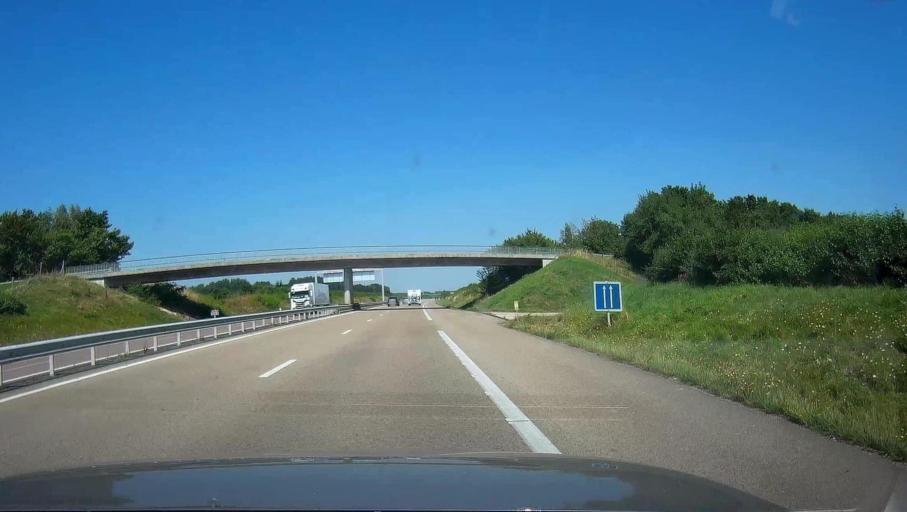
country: FR
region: Champagne-Ardenne
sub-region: Departement de l'Aube
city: Verrieres
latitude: 48.2411
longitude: 4.1713
